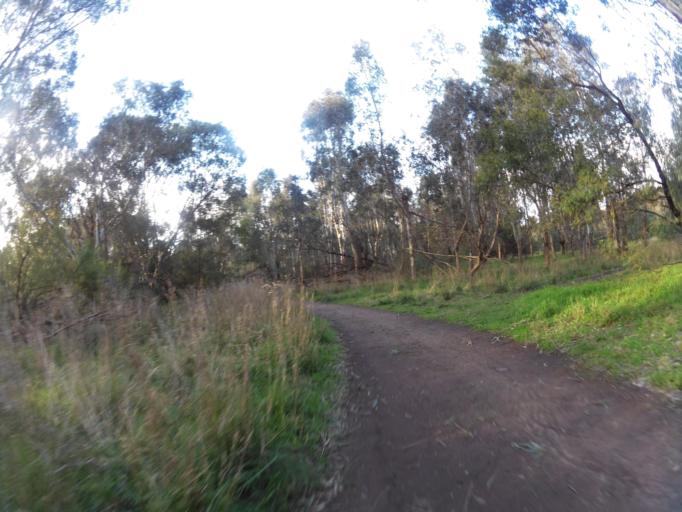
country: AU
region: Victoria
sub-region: Banyule
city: Viewbank
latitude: -37.7513
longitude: 145.0926
